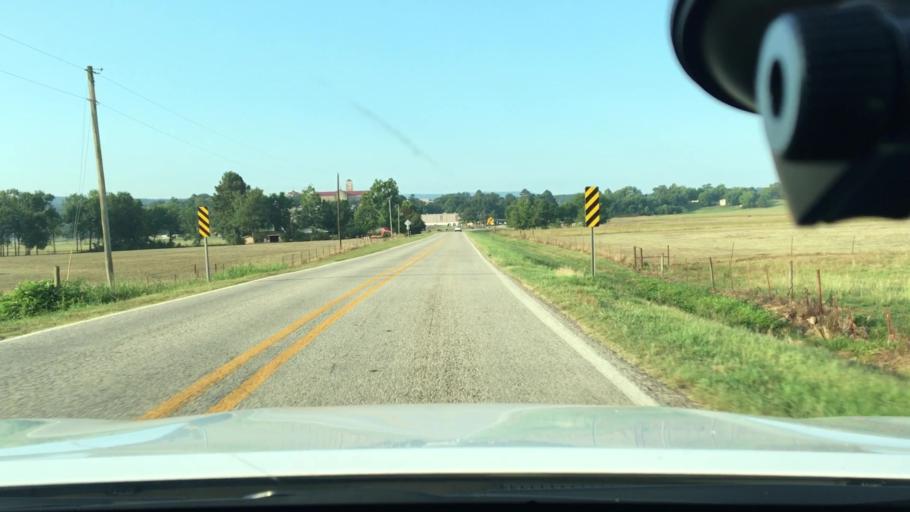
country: US
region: Arkansas
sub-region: Logan County
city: Paris
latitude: 35.3079
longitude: -93.6327
